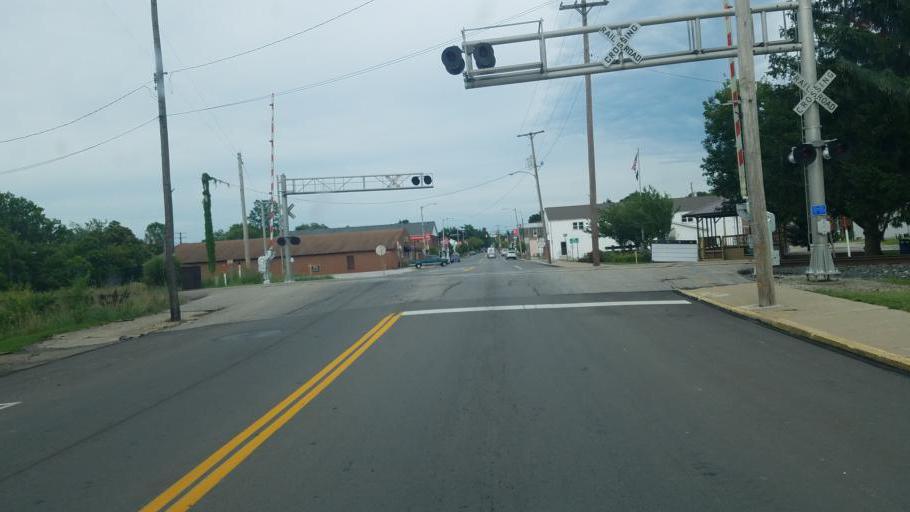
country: US
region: Ohio
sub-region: Morrow County
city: Cardington
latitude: 40.5004
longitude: -82.8964
